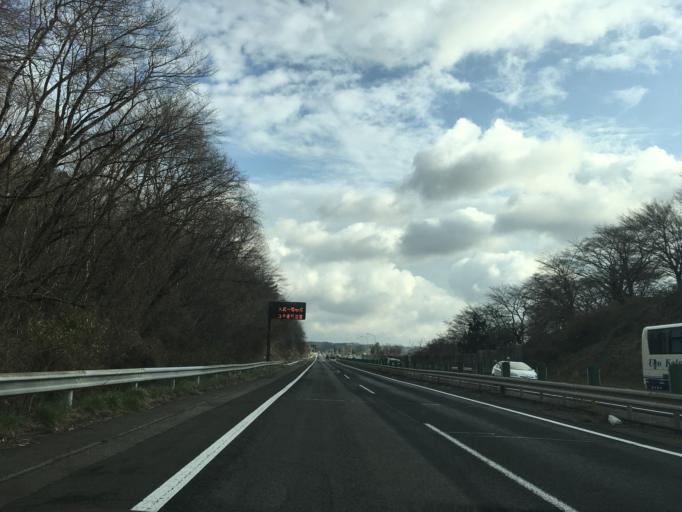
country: JP
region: Miyagi
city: Tomiya
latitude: 38.4409
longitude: 140.9150
